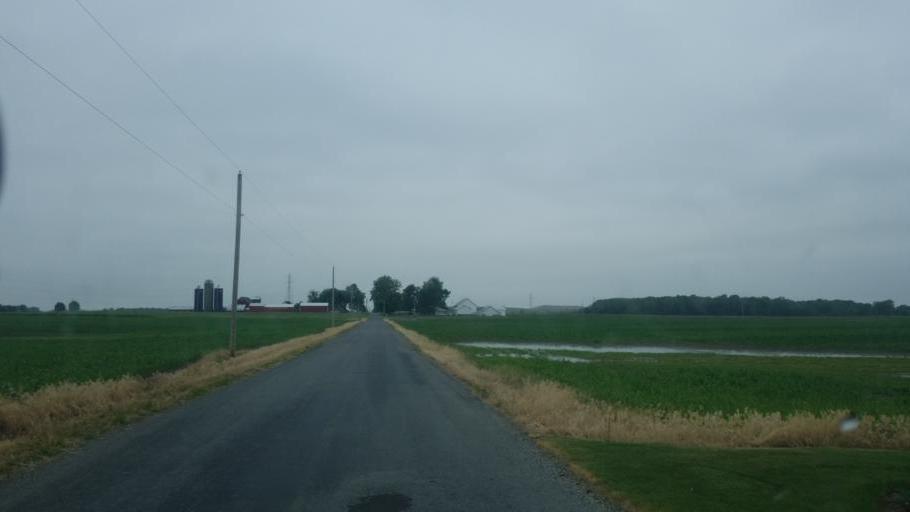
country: US
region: Indiana
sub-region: Marshall County
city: Bremen
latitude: 41.4938
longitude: -86.1330
